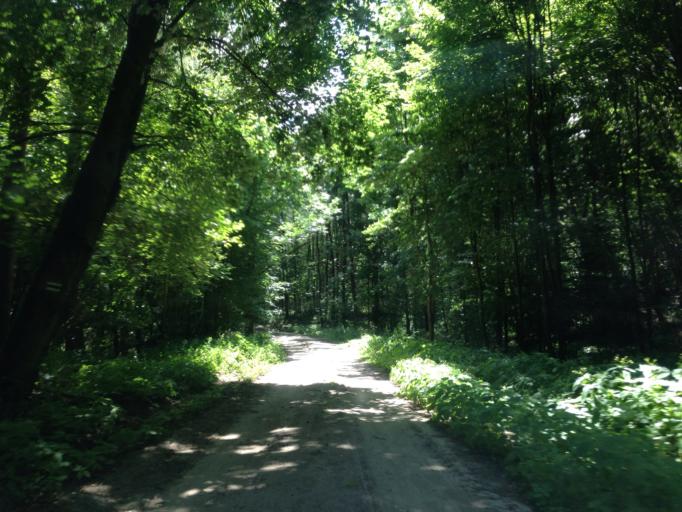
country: PL
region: Kujawsko-Pomorskie
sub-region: Powiat brodnicki
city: Gorzno
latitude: 53.2215
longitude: 19.6516
